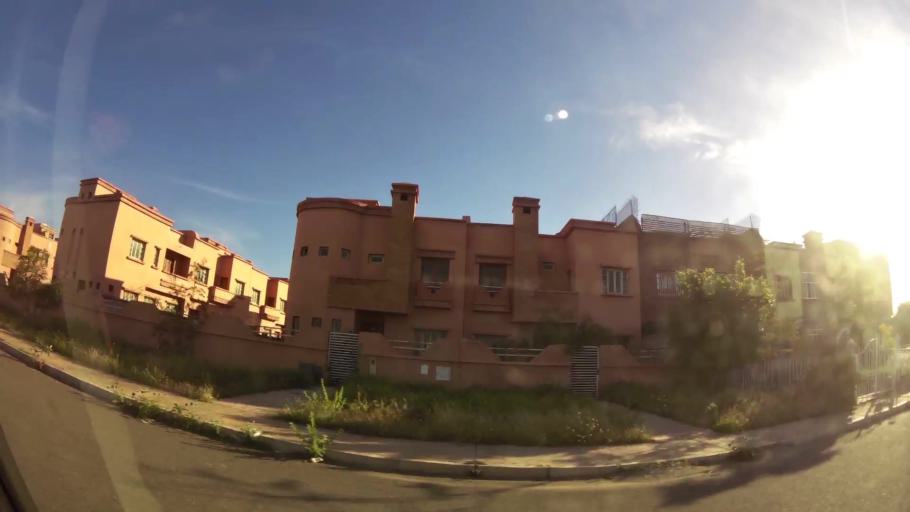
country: MA
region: Marrakech-Tensift-Al Haouz
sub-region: Marrakech
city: Marrakesh
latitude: 31.7589
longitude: -8.1060
